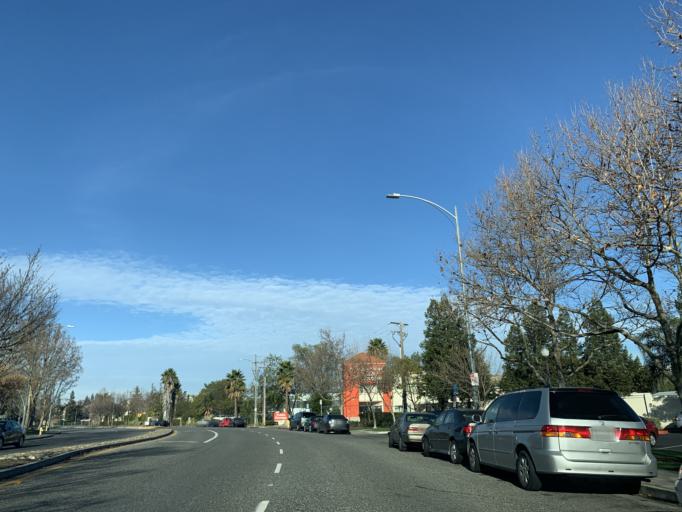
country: US
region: California
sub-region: Santa Clara County
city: Seven Trees
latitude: 37.2760
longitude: -121.8504
